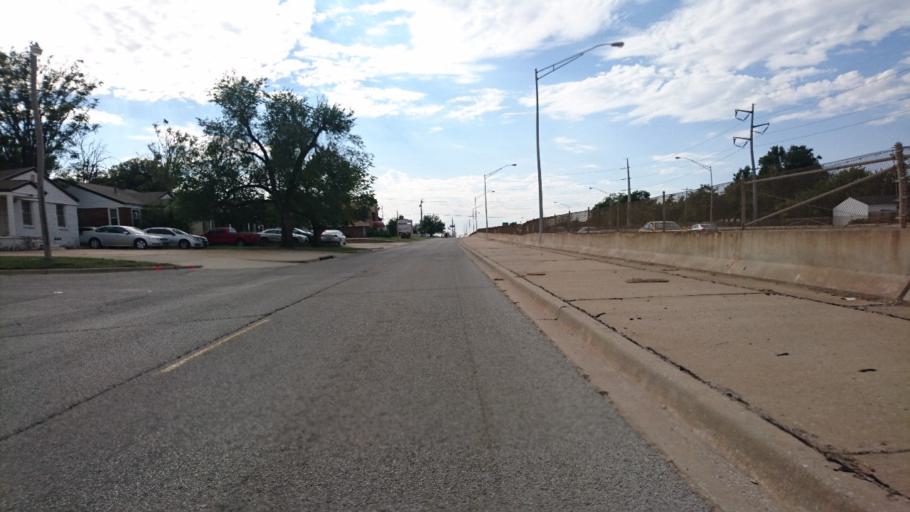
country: US
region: Oklahoma
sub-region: Oklahoma County
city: Nichols Hills
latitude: 35.5112
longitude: -97.5578
